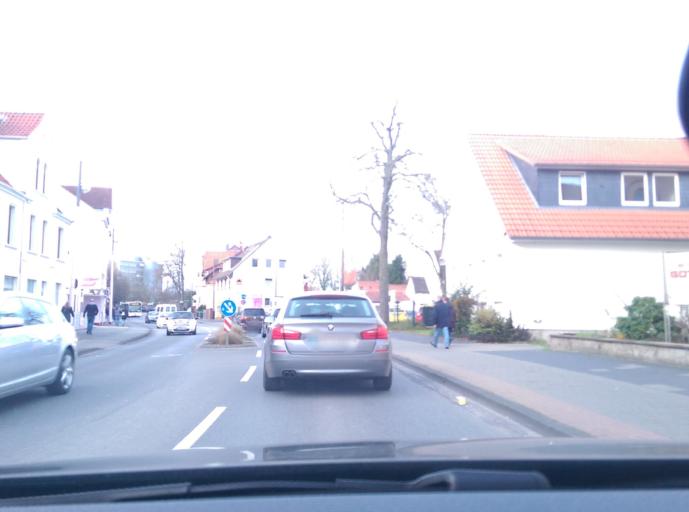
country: DE
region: Lower Saxony
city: Celle
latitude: 52.6158
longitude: 10.0786
